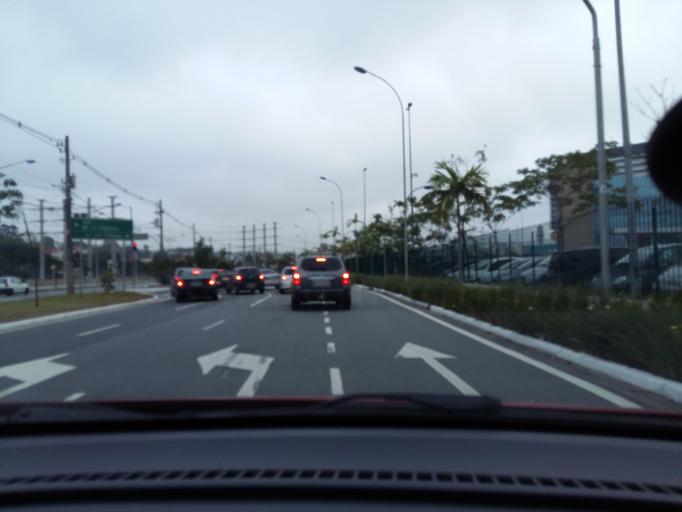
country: BR
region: Sao Paulo
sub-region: Sao Caetano Do Sul
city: Sao Caetano do Sul
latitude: -23.6276
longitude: -46.5810
